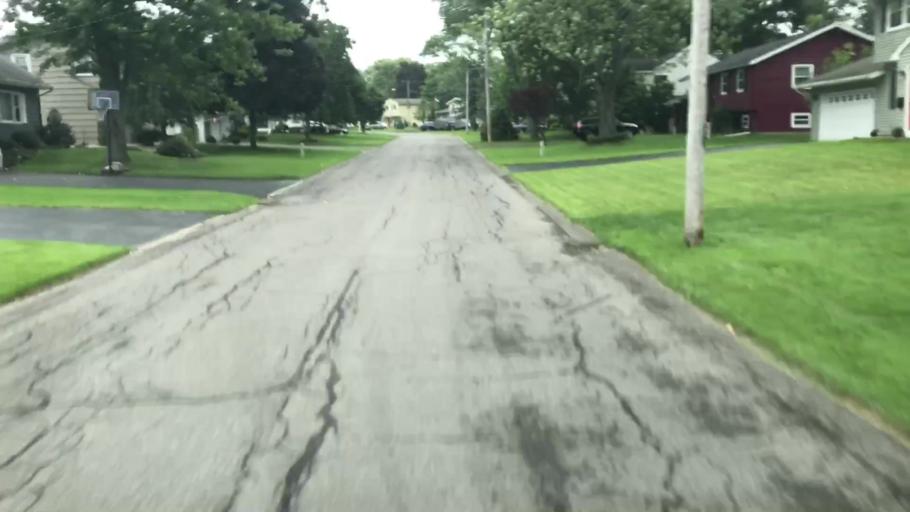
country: US
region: New York
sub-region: Onondaga County
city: Liverpool
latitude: 43.1377
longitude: -76.2191
